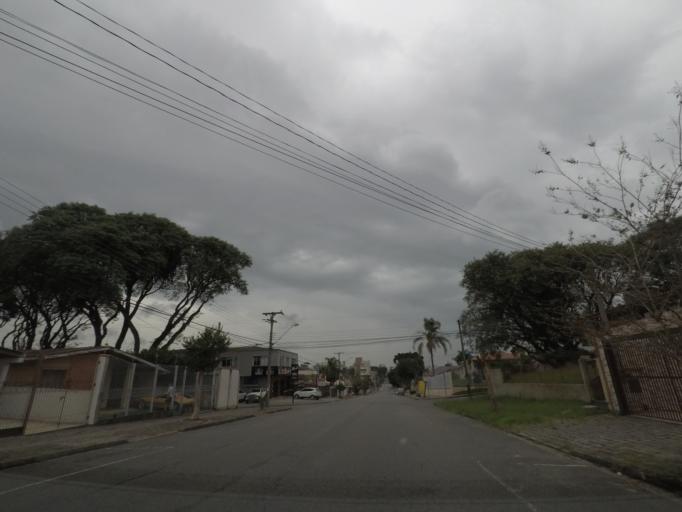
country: BR
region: Parana
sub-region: Curitiba
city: Curitiba
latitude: -25.4613
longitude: -49.2617
